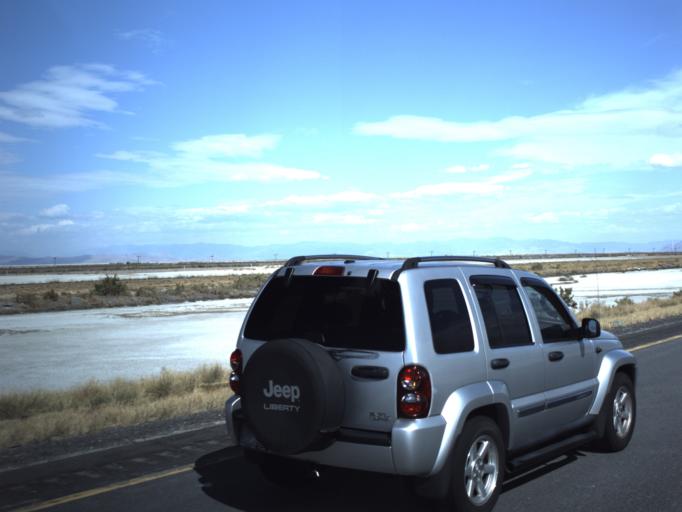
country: US
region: Utah
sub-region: Tooele County
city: Grantsville
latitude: 40.7038
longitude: -112.5076
